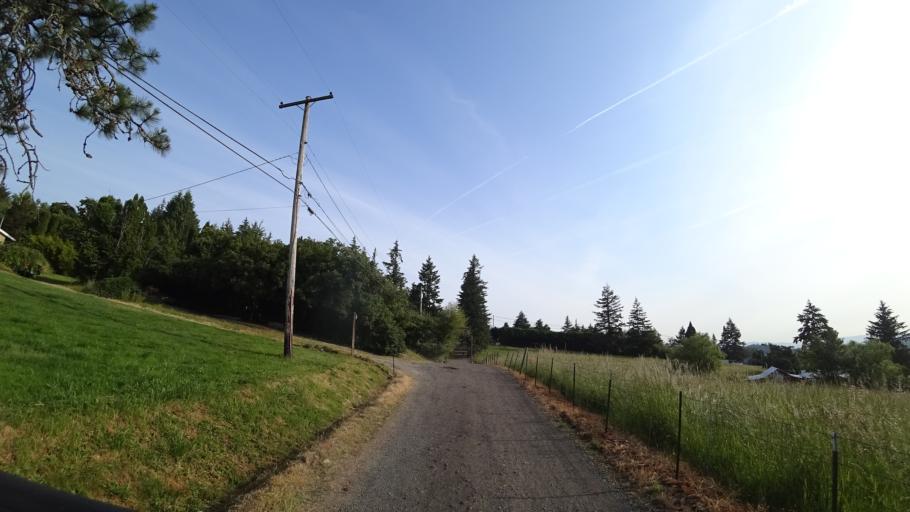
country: US
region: Oregon
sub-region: Clackamas County
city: Happy Valley
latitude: 45.4596
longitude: -122.5069
